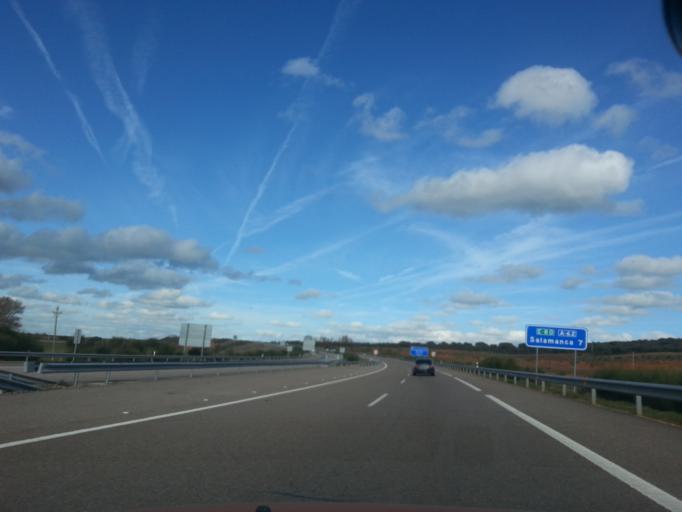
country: ES
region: Castille and Leon
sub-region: Provincia de Salamanca
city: Doninos de Salamanca
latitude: 40.9361
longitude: -5.7800
